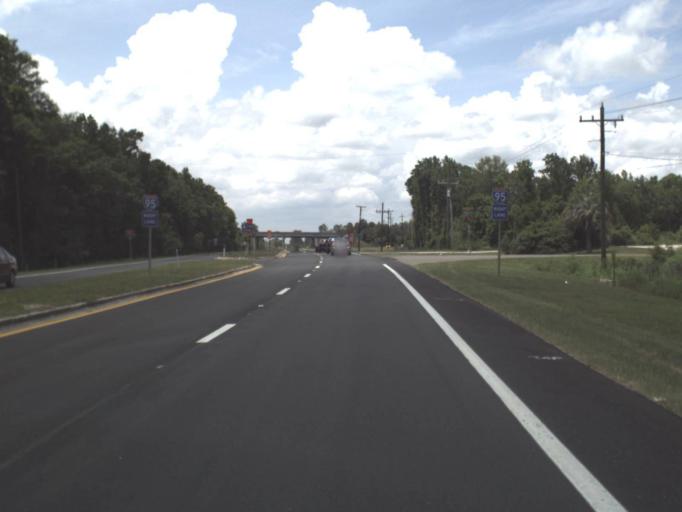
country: US
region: Georgia
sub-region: Camden County
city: Kingsland
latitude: 30.7075
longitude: -81.6686
